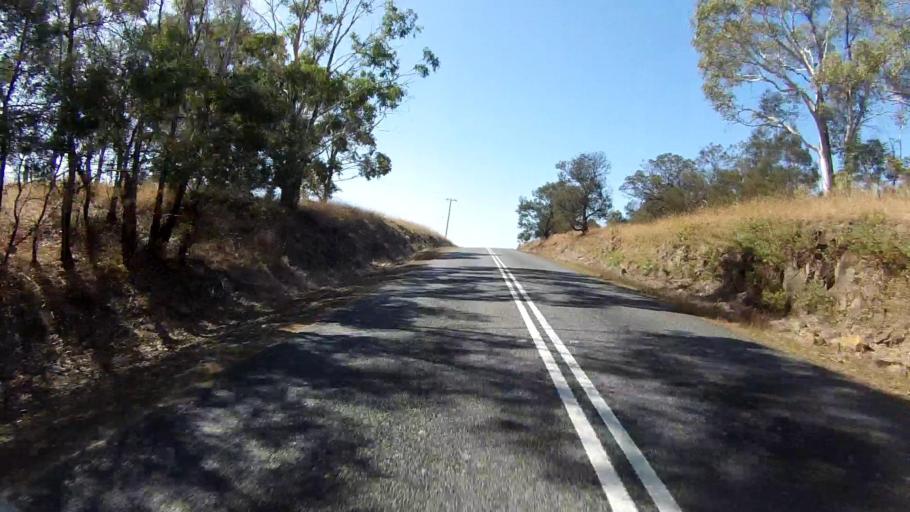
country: AU
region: Tasmania
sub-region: Sorell
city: Sorell
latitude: -42.2846
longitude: 147.9976
